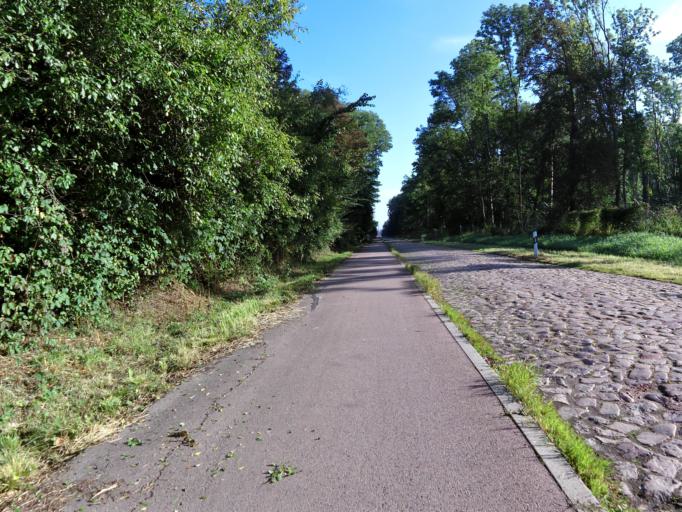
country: DE
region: Saxony-Anhalt
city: Coswig
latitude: 51.8653
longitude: 12.4408
